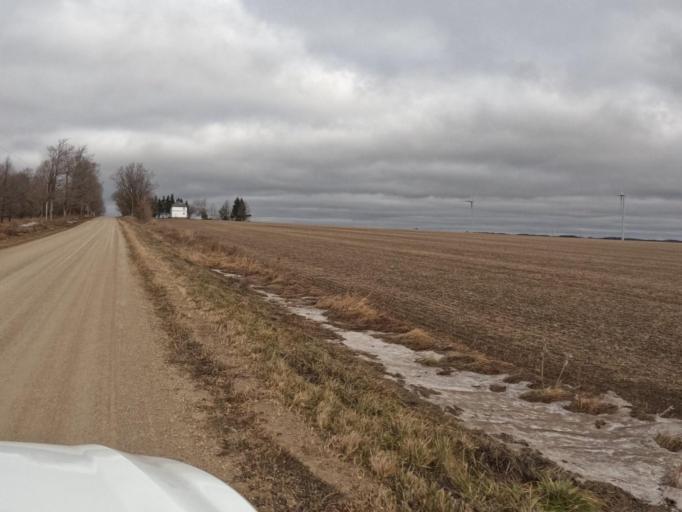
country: CA
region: Ontario
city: Shelburne
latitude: 43.9947
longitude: -80.4082
